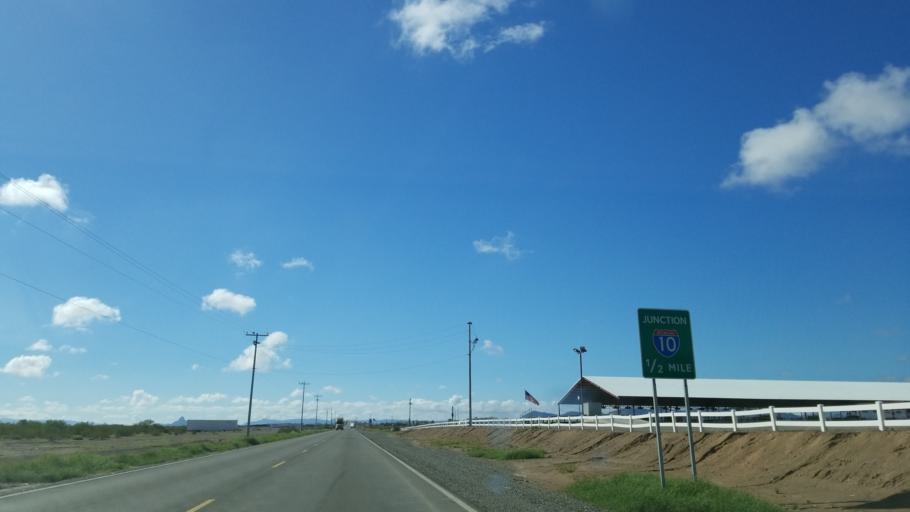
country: US
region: Arizona
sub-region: La Paz County
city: Salome
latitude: 33.6425
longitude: -113.7672
